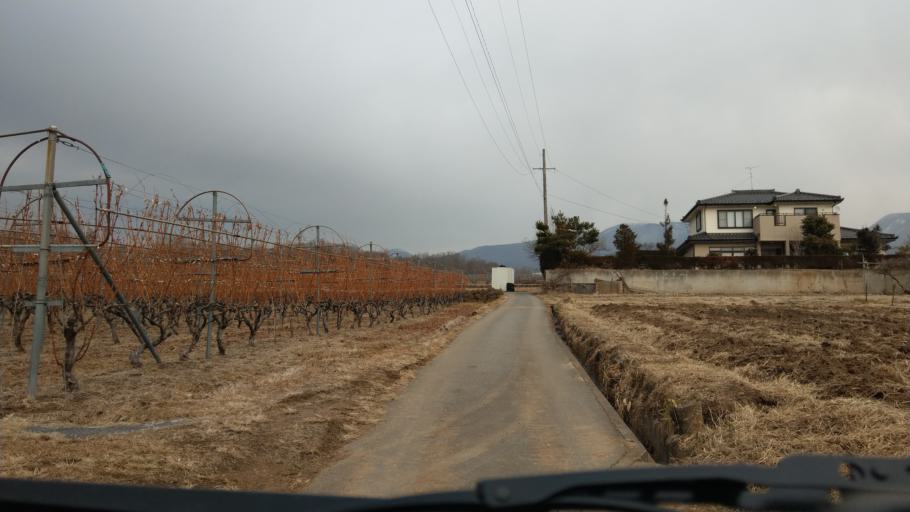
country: JP
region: Nagano
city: Komoro
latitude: 36.3405
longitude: 138.3979
